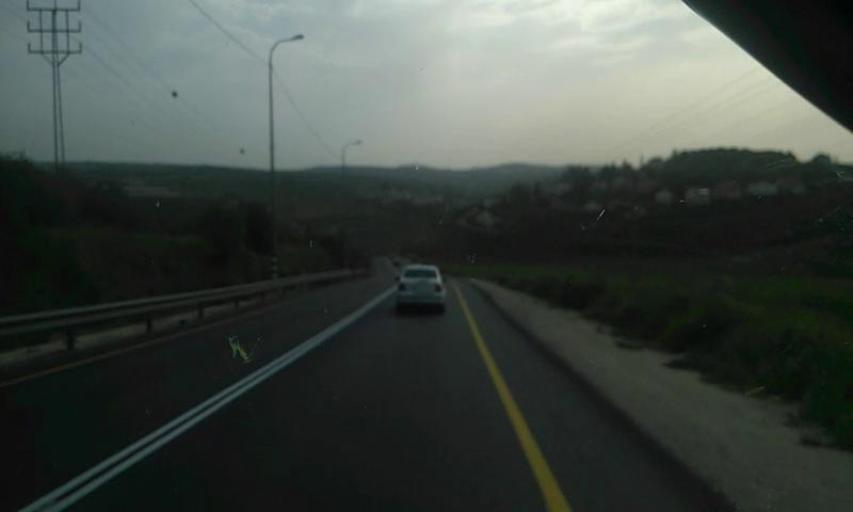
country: PS
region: West Bank
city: Jit
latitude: 32.2146
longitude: 35.1670
